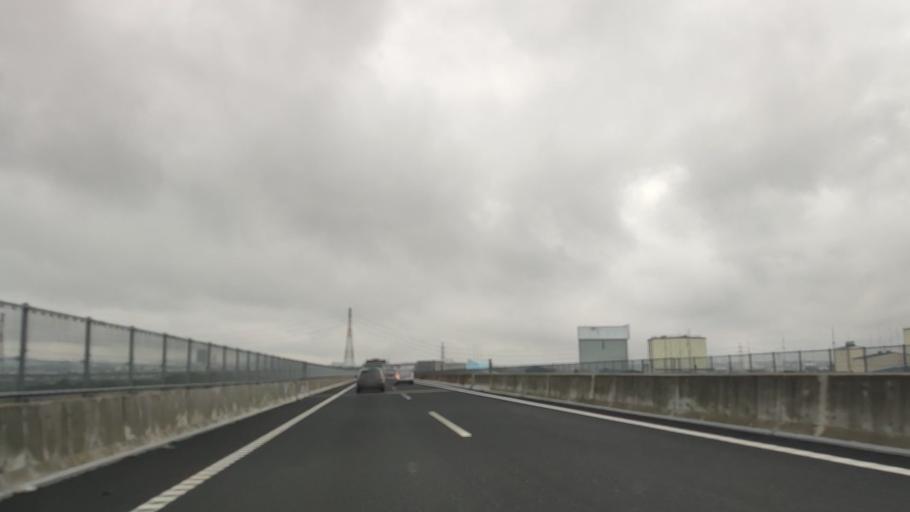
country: JP
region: Kanagawa
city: Atsugi
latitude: 35.3970
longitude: 139.3768
